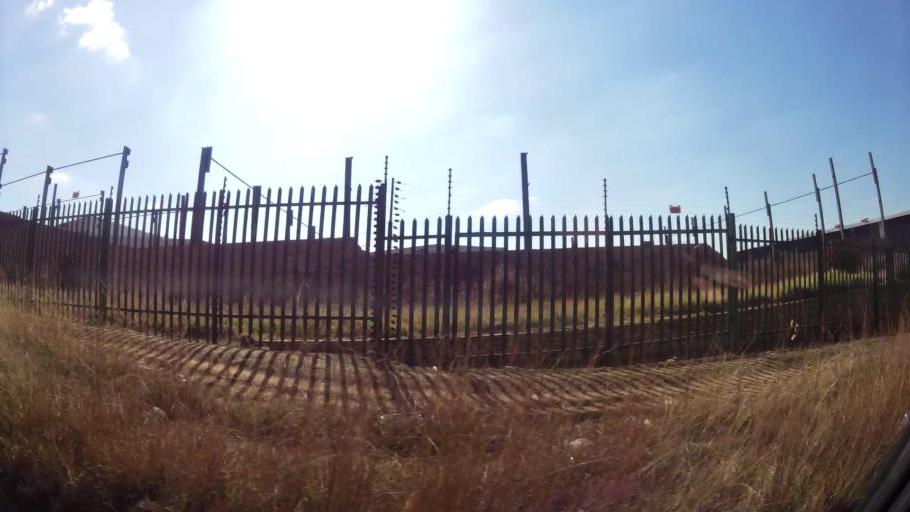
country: ZA
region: Gauteng
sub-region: West Rand District Municipality
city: Muldersdriseloop
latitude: -26.0328
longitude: 27.9429
